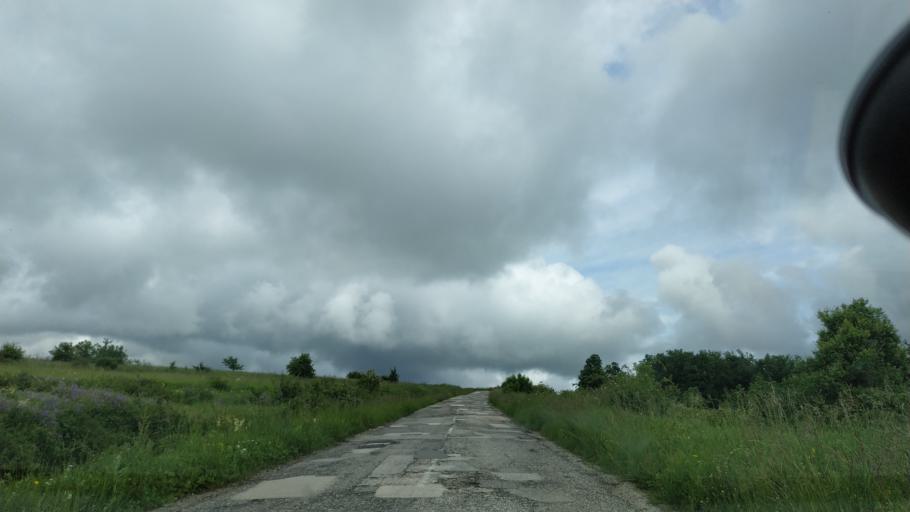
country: RS
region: Central Serbia
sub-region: Zajecarski Okrug
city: Soko Banja
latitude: 43.6966
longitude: 21.9387
